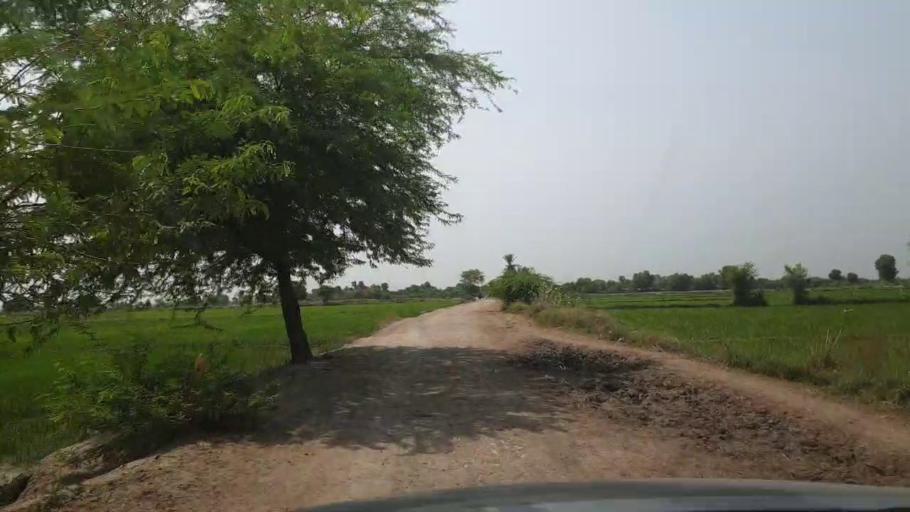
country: PK
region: Sindh
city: Madeji
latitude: 27.8008
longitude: 68.5392
